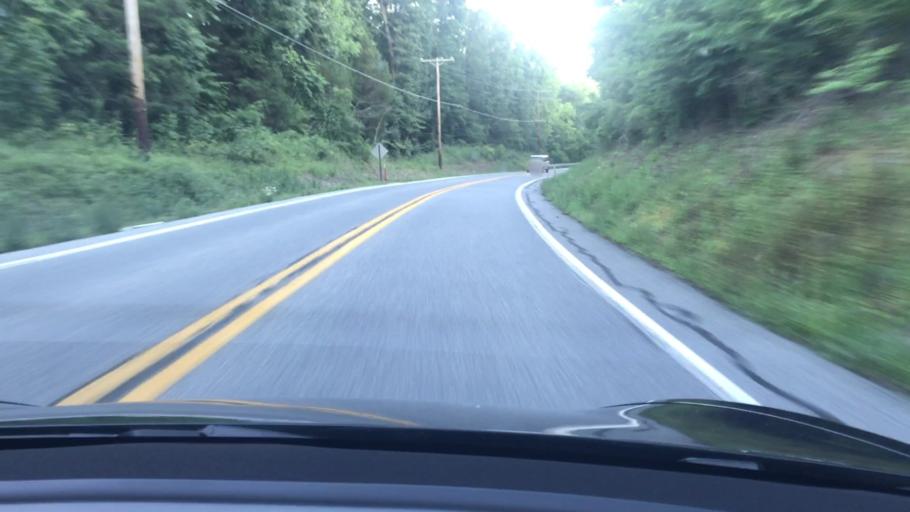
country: US
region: Pennsylvania
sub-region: York County
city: Dover
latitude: 40.0910
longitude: -76.8692
